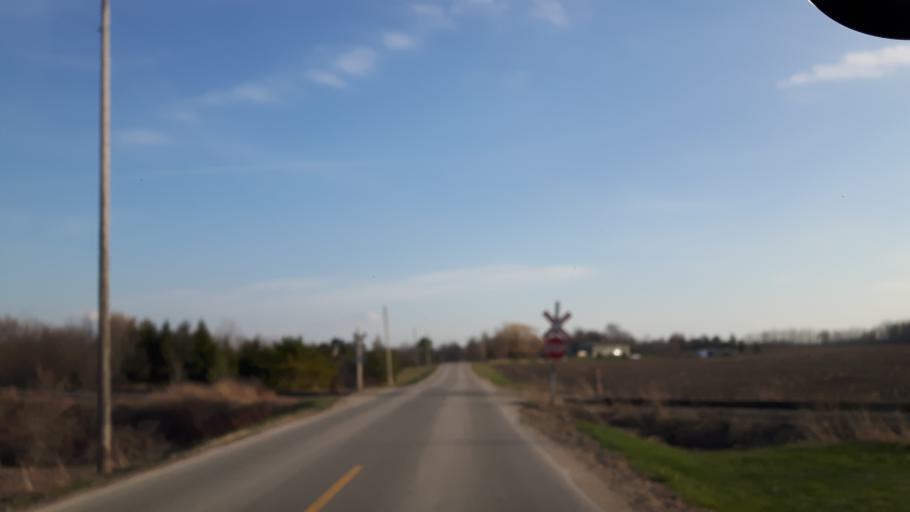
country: CA
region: Ontario
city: Goderich
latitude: 43.6863
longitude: -81.6645
